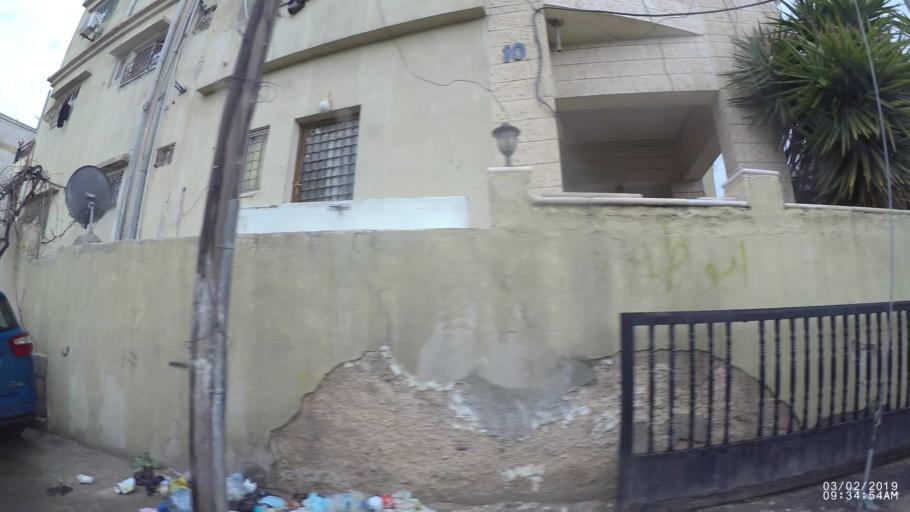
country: JO
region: Amman
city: Amman
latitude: 31.9481
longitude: 35.9116
